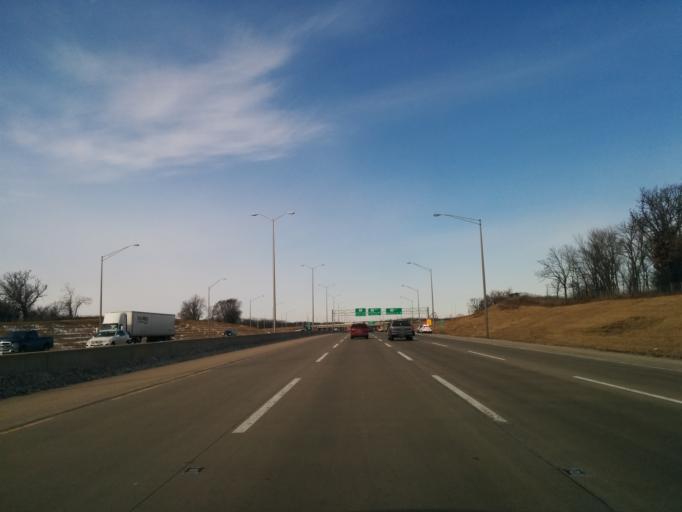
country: US
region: Illinois
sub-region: Lake County
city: Gurnee
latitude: 42.3410
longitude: -87.9191
